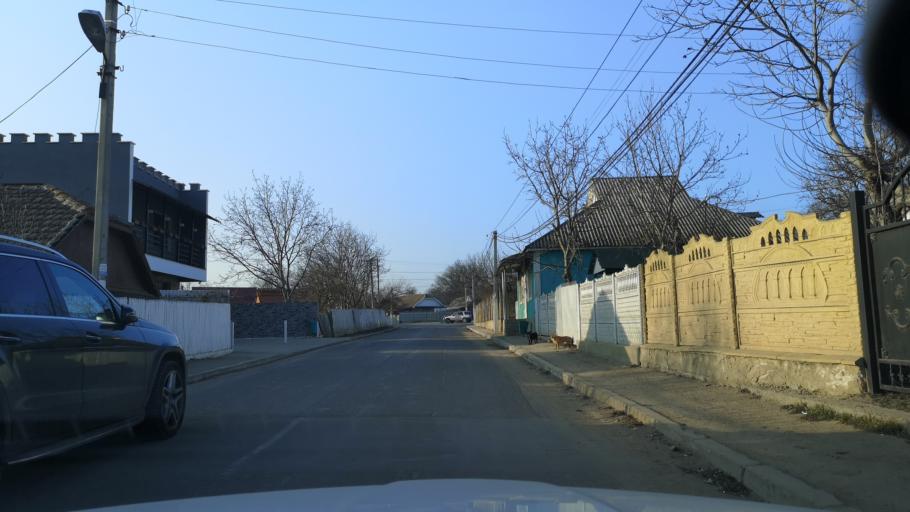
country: MD
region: Stinga Nistrului
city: Bucovat
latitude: 47.1158
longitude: 28.5059
